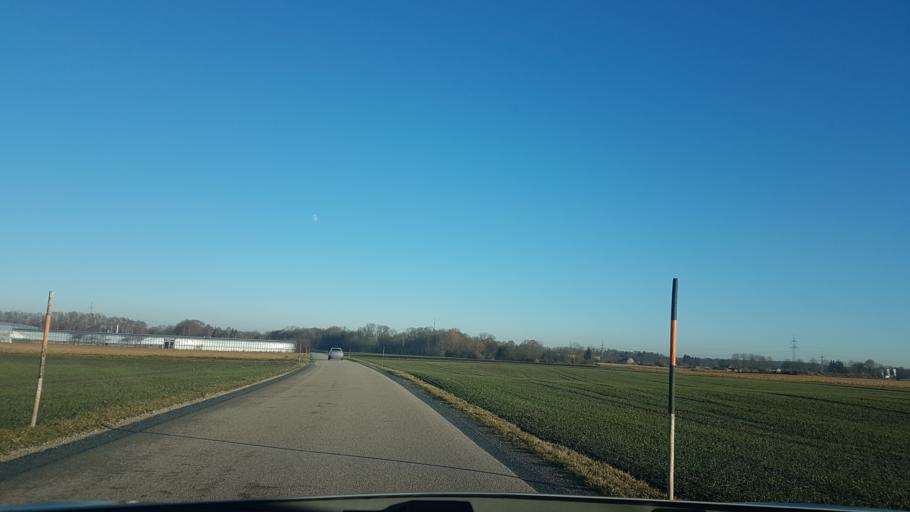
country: DE
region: Bavaria
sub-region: Upper Bavaria
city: Eichenried
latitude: 48.2802
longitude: 11.8097
